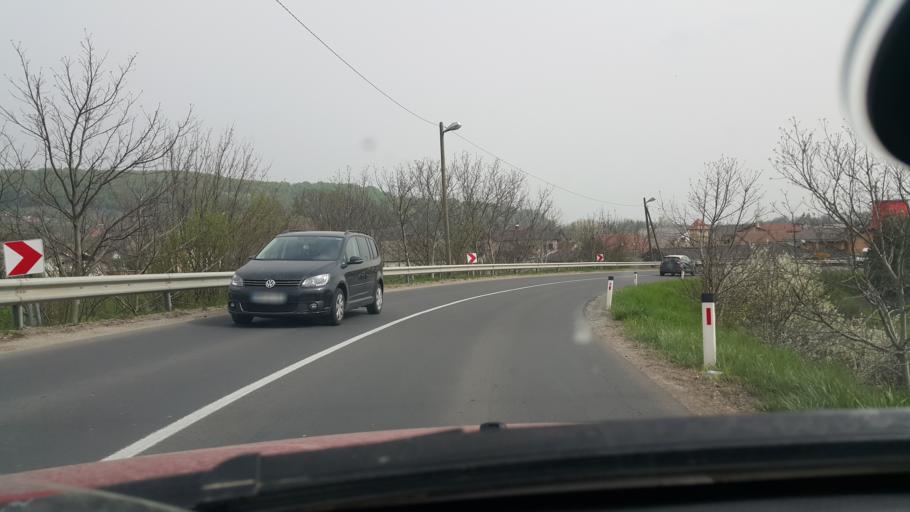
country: SI
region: Duplek
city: Zgornji Duplek
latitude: 46.5256
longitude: 15.7039
